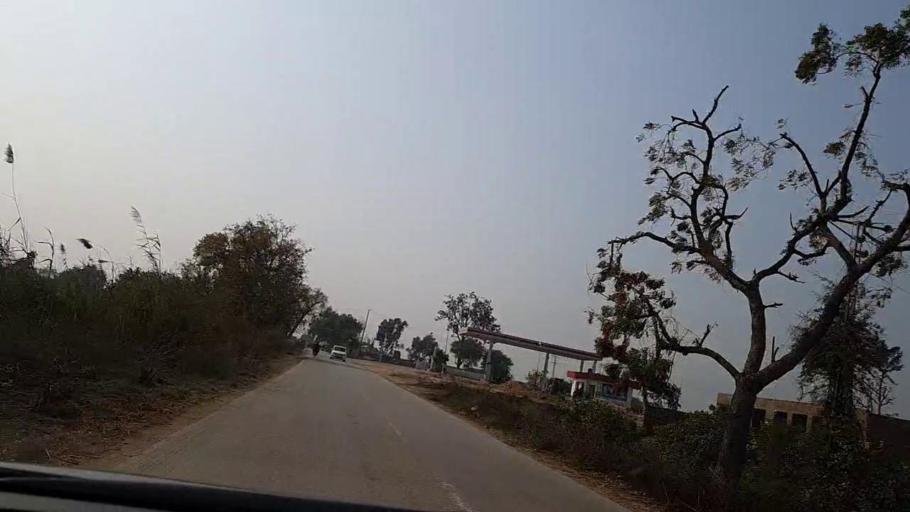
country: PK
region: Sindh
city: Sakrand
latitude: 26.1365
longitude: 68.2417
